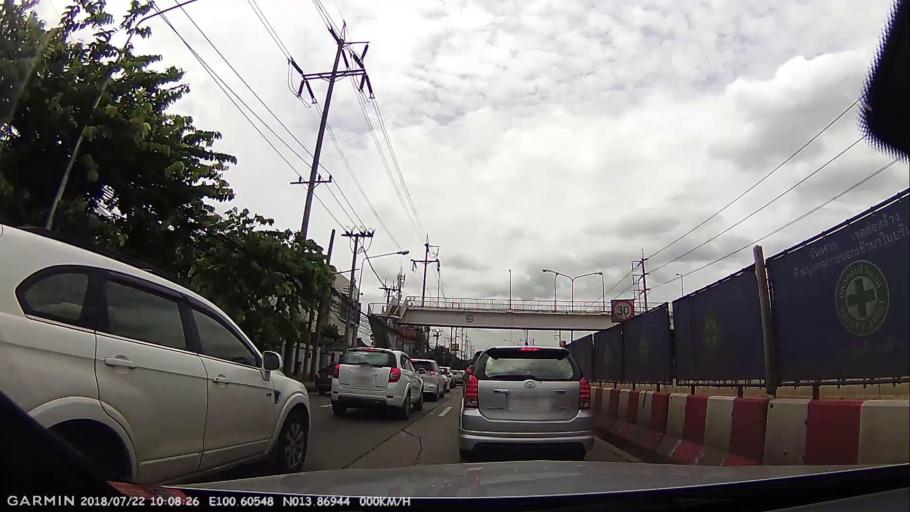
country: TH
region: Bangkok
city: Bang Khen
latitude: 13.8694
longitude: 100.6055
